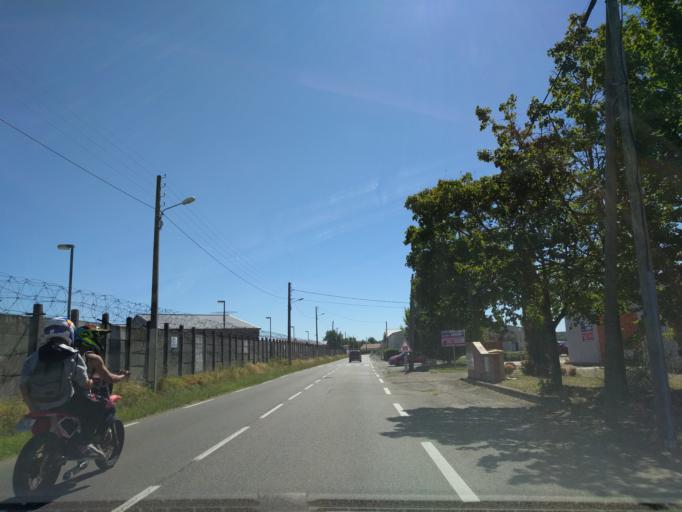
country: FR
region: Midi-Pyrenees
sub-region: Departement du Tarn-et-Garonne
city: Montauban
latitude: 44.0294
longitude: 1.3756
